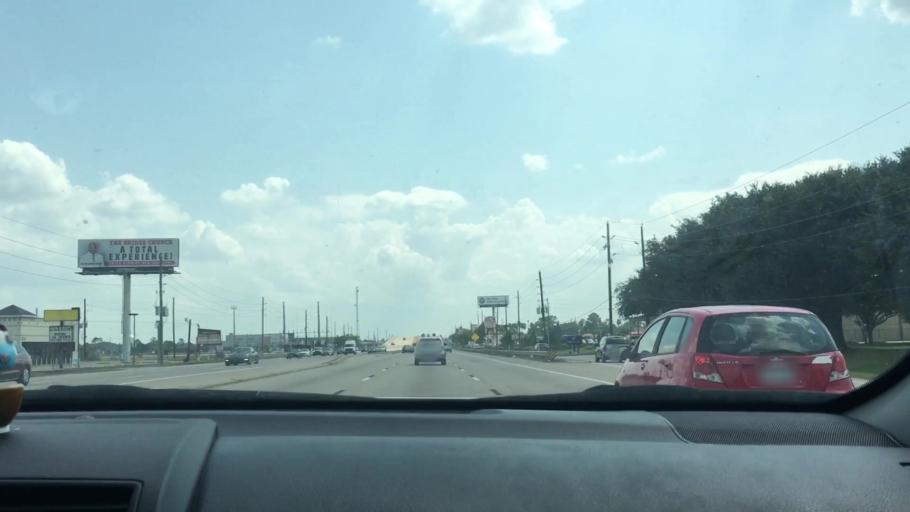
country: US
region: Texas
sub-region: Fort Bend County
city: Mission Bend
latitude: 29.7174
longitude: -95.6443
